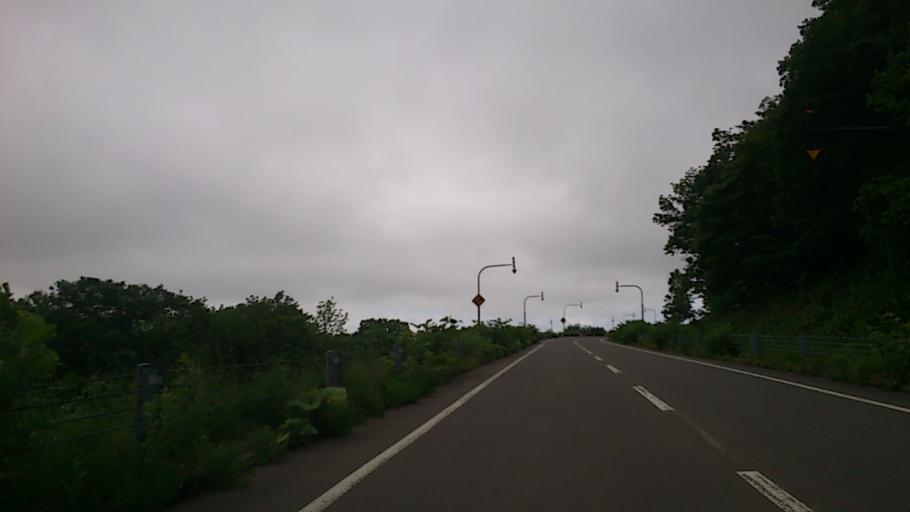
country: JP
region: Hokkaido
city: Niseko Town
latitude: 42.8566
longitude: 140.5896
